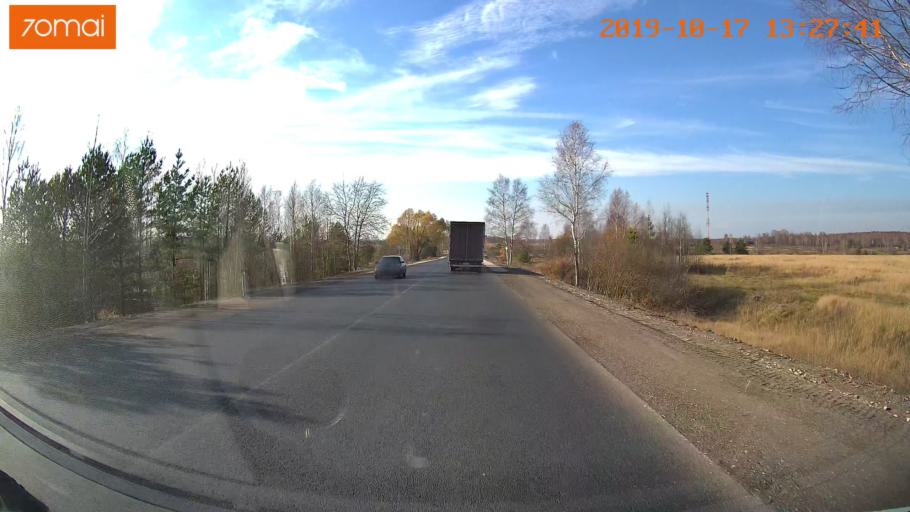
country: RU
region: Vladimir
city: Velikodvorskiy
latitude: 55.1139
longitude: 40.8893
